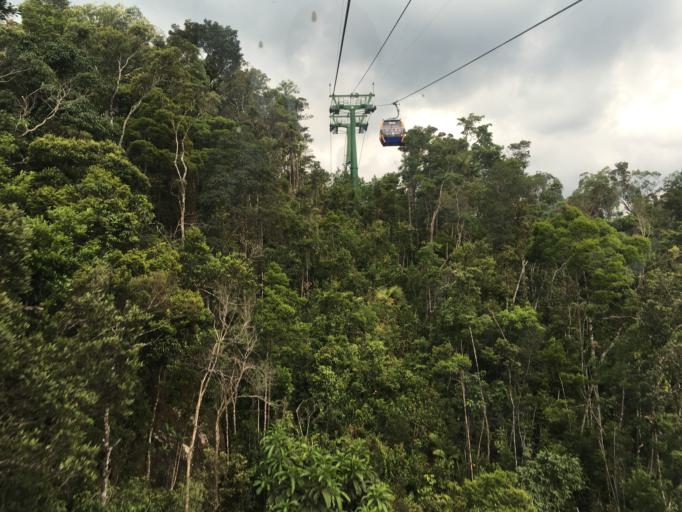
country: VN
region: Da Nang
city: Hoa Vang
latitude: 16.0153
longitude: 108.0141
